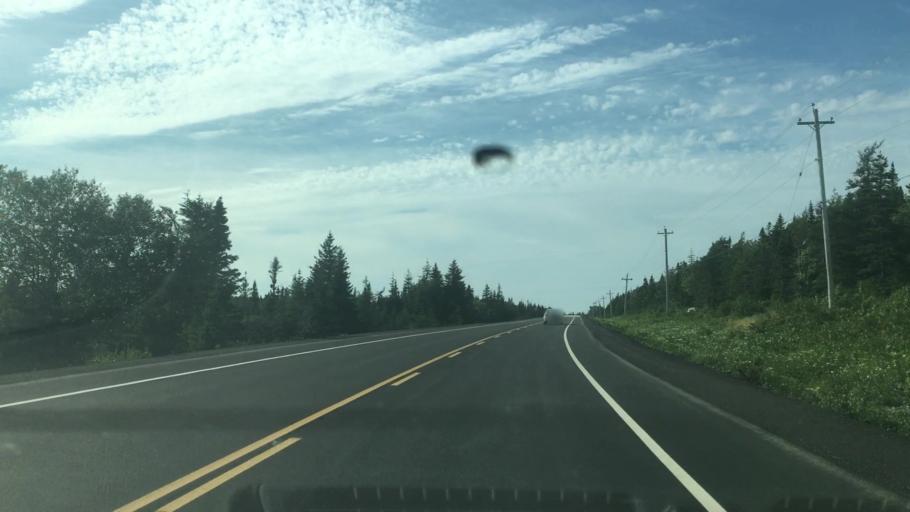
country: CA
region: Nova Scotia
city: Sydney Mines
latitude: 46.8450
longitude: -60.4080
